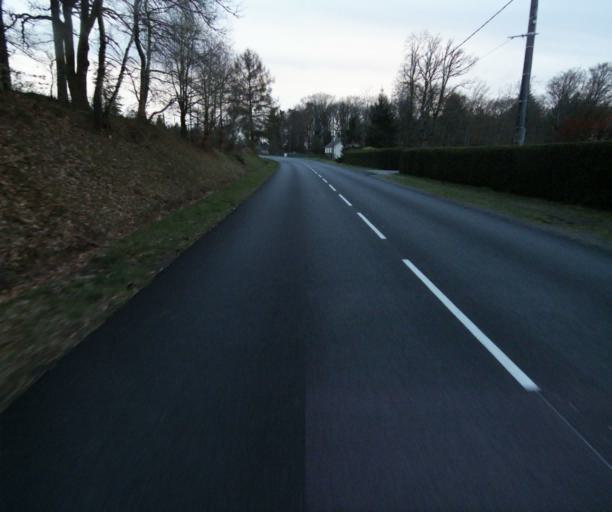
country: FR
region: Limousin
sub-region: Departement de la Correze
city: Correze
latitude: 45.3458
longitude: 1.8754
